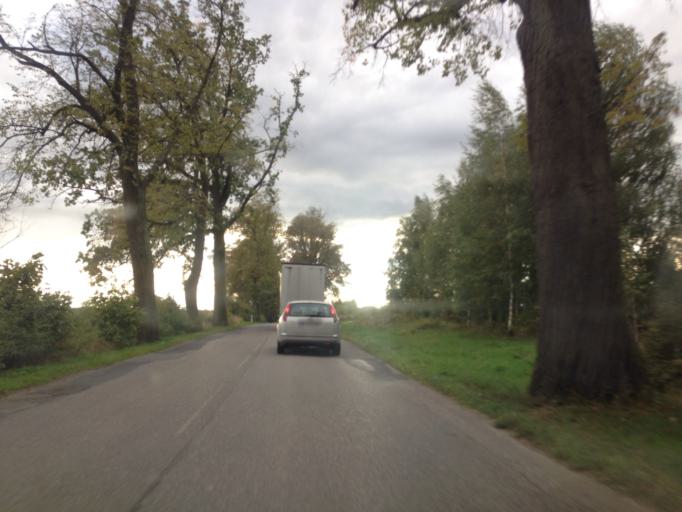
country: PL
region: Pomeranian Voivodeship
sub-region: Powiat kwidzynski
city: Kwidzyn
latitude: 53.7337
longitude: 19.0549
